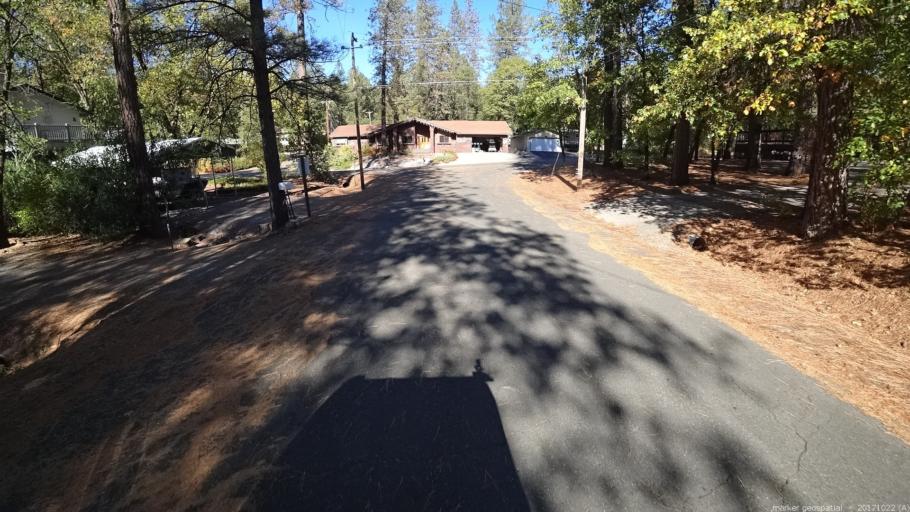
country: US
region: California
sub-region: Shasta County
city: Central Valley (historical)
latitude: 40.8866
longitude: -122.3893
